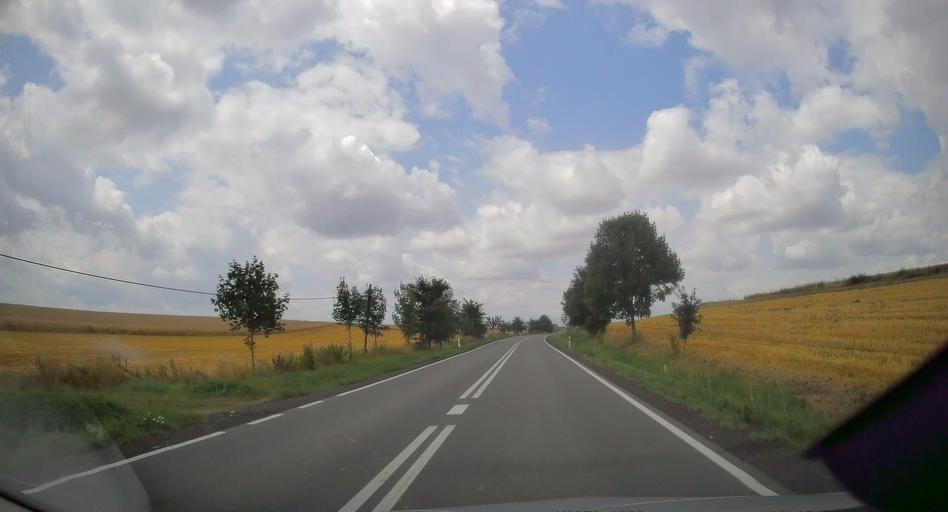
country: PL
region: Opole Voivodeship
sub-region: Powiat prudnicki
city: Raclawice Slaskie
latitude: 50.3521
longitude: 17.8074
